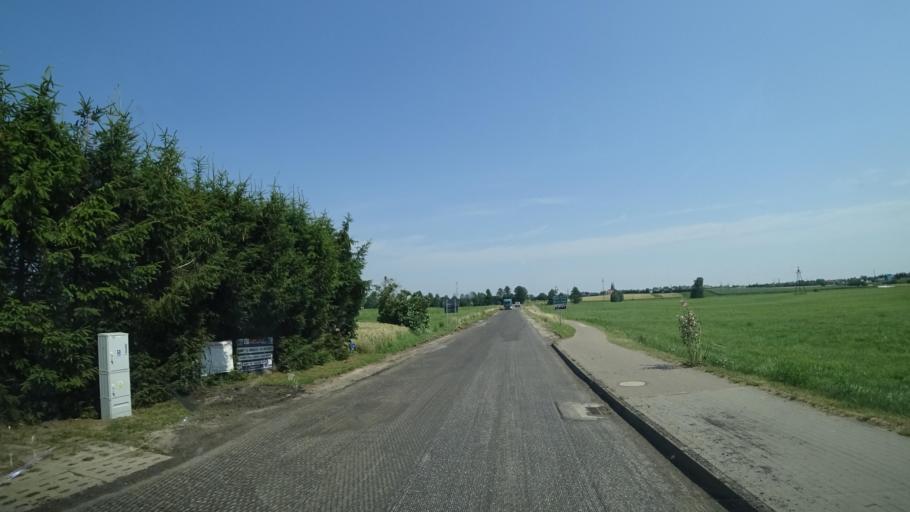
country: PL
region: Pomeranian Voivodeship
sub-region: Powiat chojnicki
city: Brusy
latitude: 53.8808
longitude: 17.6957
